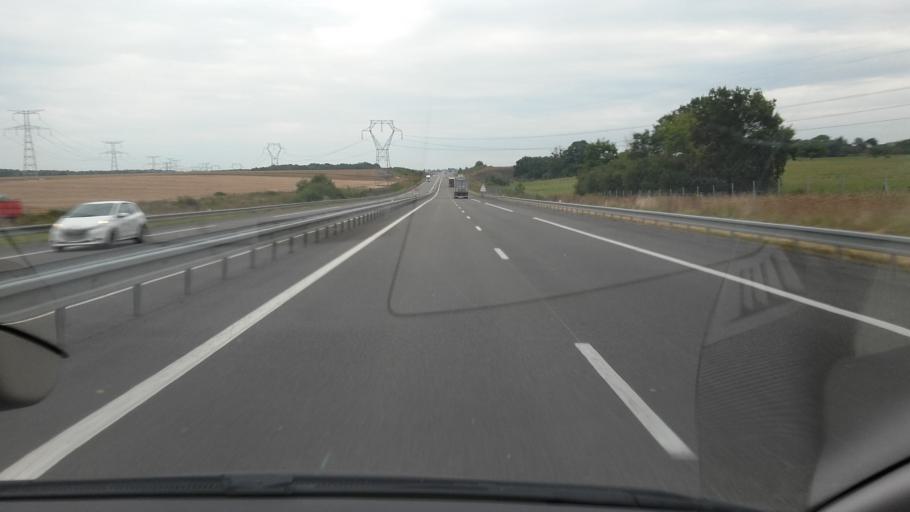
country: FR
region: Champagne-Ardenne
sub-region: Departement des Ardennes
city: Rethel
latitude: 49.5677
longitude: 4.4715
